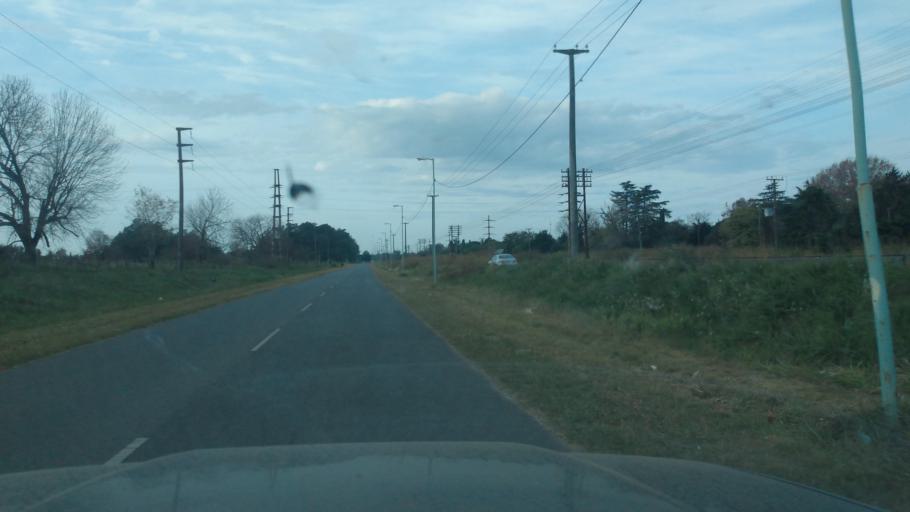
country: AR
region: Buenos Aires
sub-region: Partido de Lujan
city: Lujan
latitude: -34.5896
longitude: -59.1413
